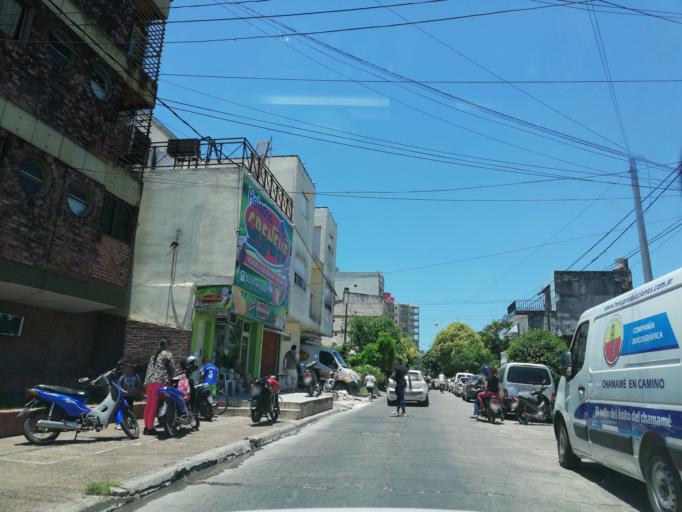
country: AR
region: Corrientes
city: Corrientes
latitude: -27.4650
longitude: -58.8261
